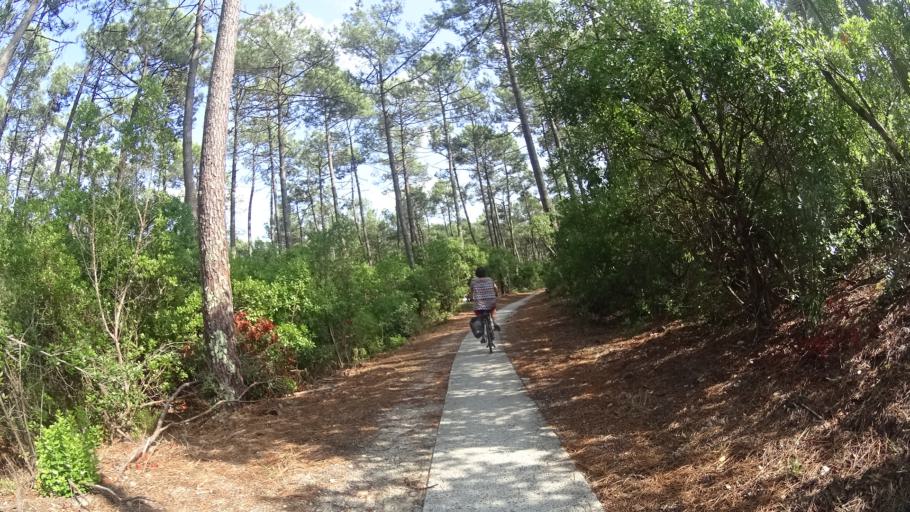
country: FR
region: Aquitaine
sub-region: Departement de la Gironde
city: Lacanau
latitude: 44.9646
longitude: -1.1738
